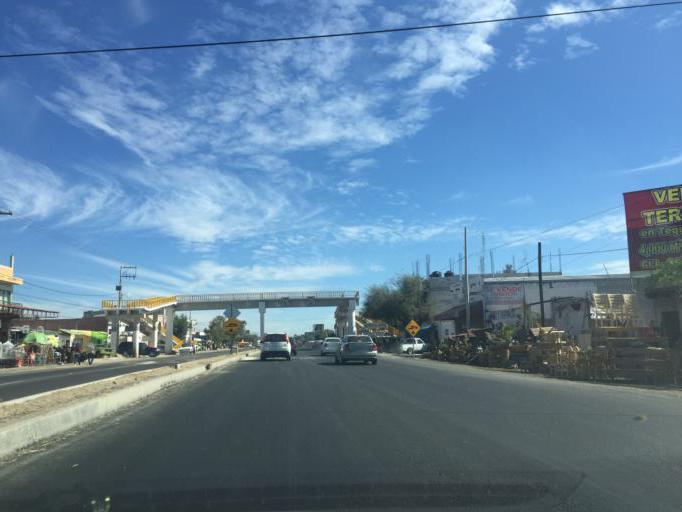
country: MX
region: Queretaro
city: San Nicolas
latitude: 20.4973
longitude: -99.9301
